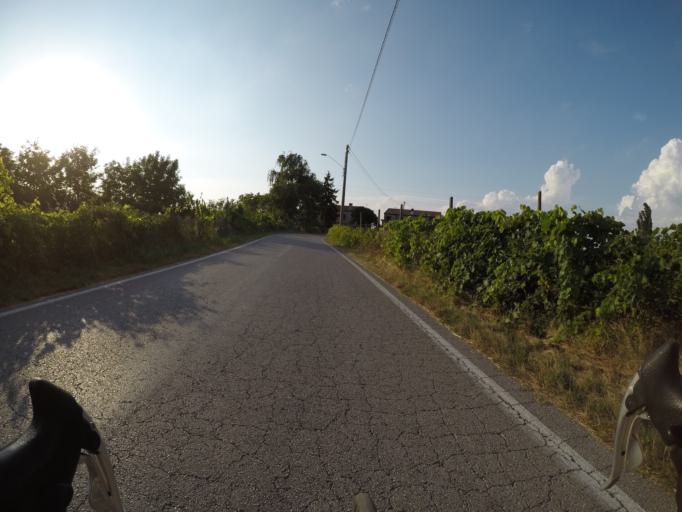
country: IT
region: Veneto
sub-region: Provincia di Rovigo
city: San Bellino
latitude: 45.0469
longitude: 11.5866
